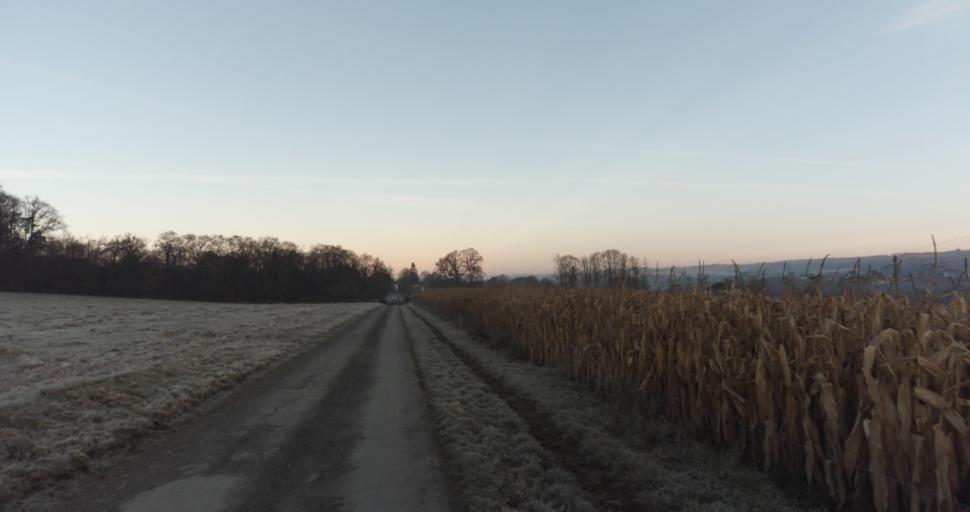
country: FR
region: Limousin
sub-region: Departement de la Haute-Vienne
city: Aixe-sur-Vienne
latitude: 45.8177
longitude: 1.1566
